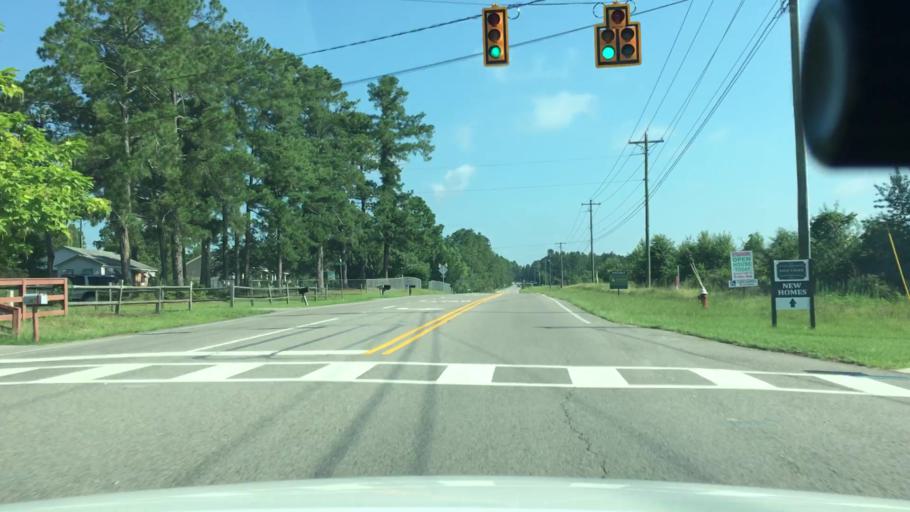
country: US
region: South Carolina
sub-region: Aiken County
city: Graniteville
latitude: 33.5841
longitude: -81.8362
